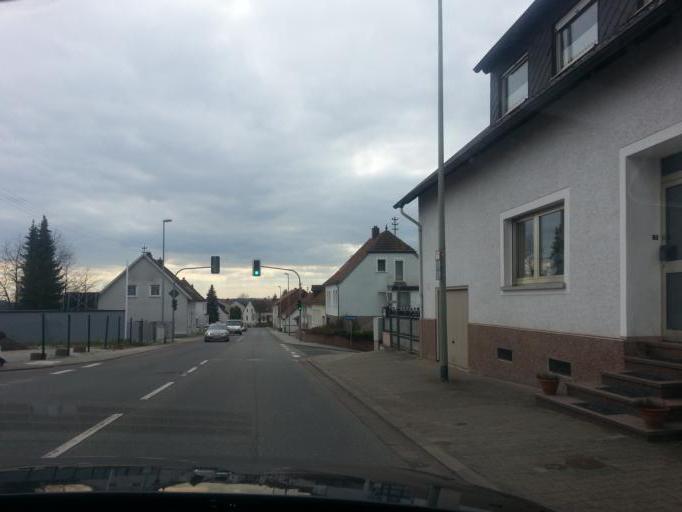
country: DE
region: Saarland
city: Bexbach
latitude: 49.3656
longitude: 7.2669
